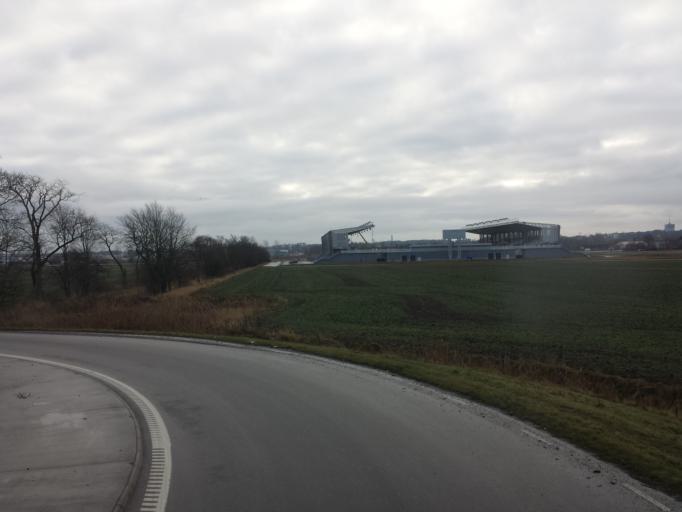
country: SE
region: OEstergoetland
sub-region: Linkopings Kommun
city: Linkoping
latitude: 58.4216
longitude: 15.6498
